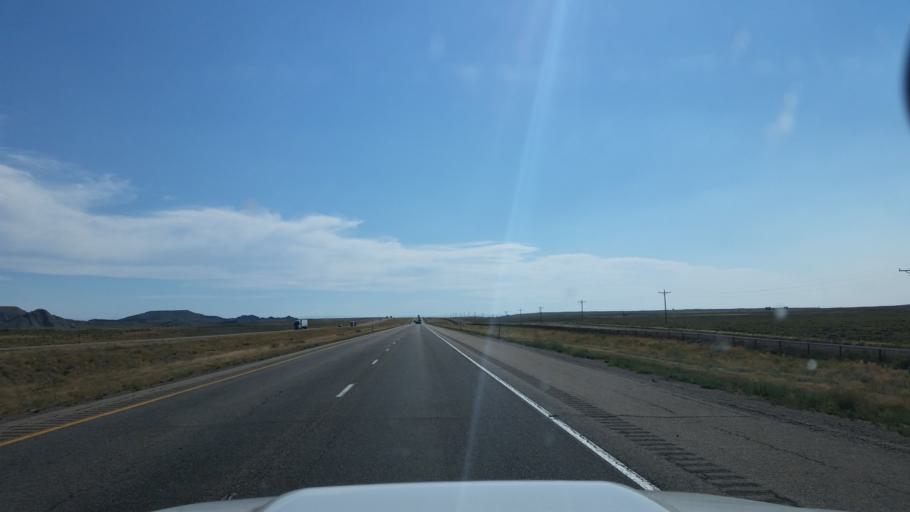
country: US
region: Wyoming
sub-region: Uinta County
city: Lyman
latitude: 41.4460
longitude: -110.0825
